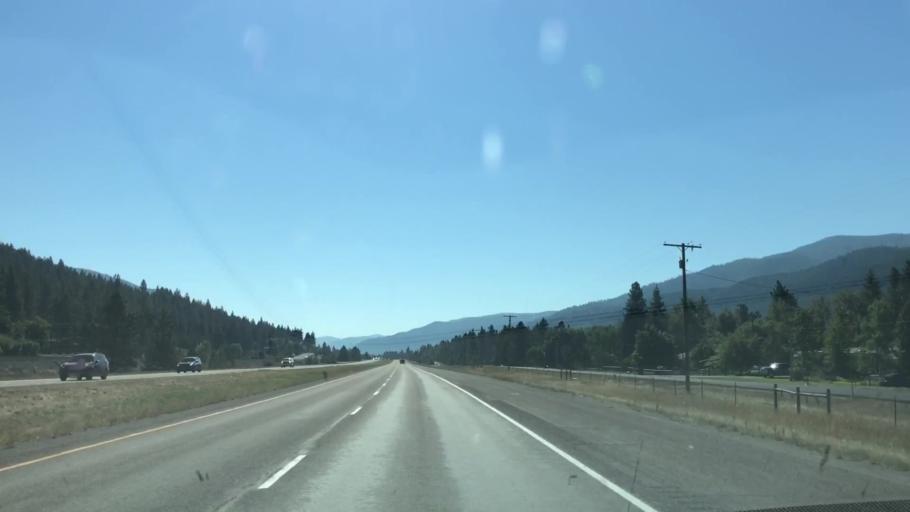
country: US
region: Montana
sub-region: Missoula County
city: Bonner-West Riverside
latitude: 46.8521
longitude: -113.8546
